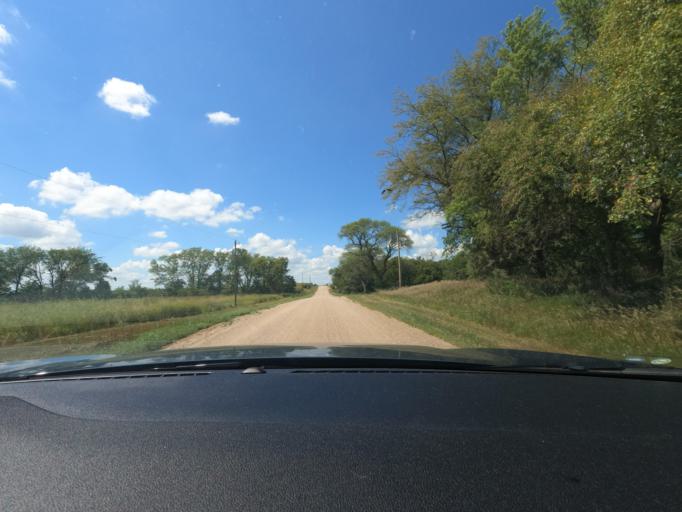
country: US
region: Nebraska
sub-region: Saunders County
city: Wahoo
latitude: 41.2492
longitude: -96.5479
